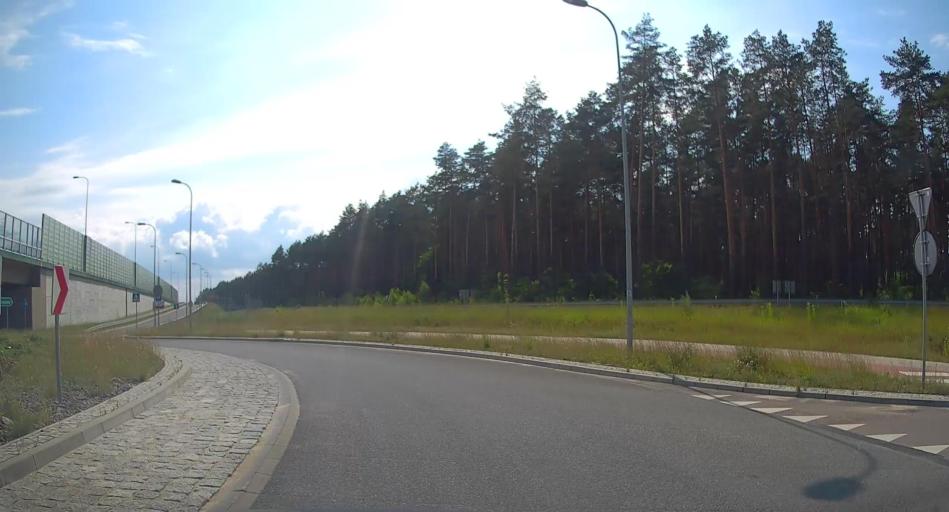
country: PL
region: Masovian Voivodeship
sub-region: Powiat wyszkowski
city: Dlugosiodlo
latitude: 52.7219
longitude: 21.7089
